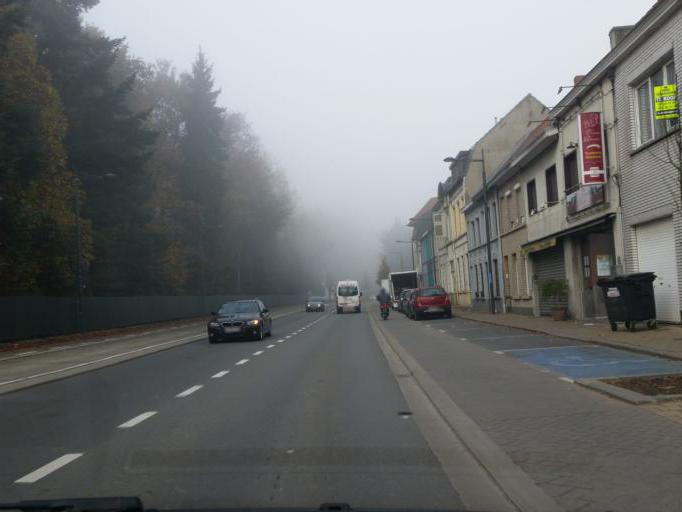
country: BE
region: Flanders
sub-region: Provincie Oost-Vlaanderen
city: Melle
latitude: 51.0039
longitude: 3.7997
